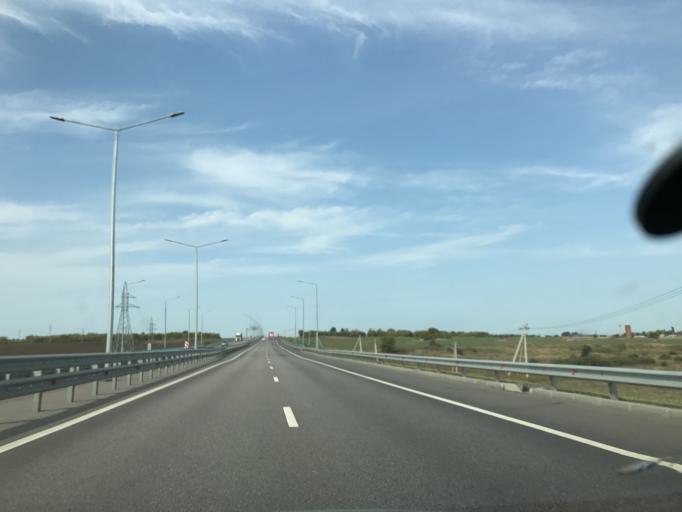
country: RU
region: Voronezj
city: Kashirskoye
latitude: 51.4914
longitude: 39.5303
